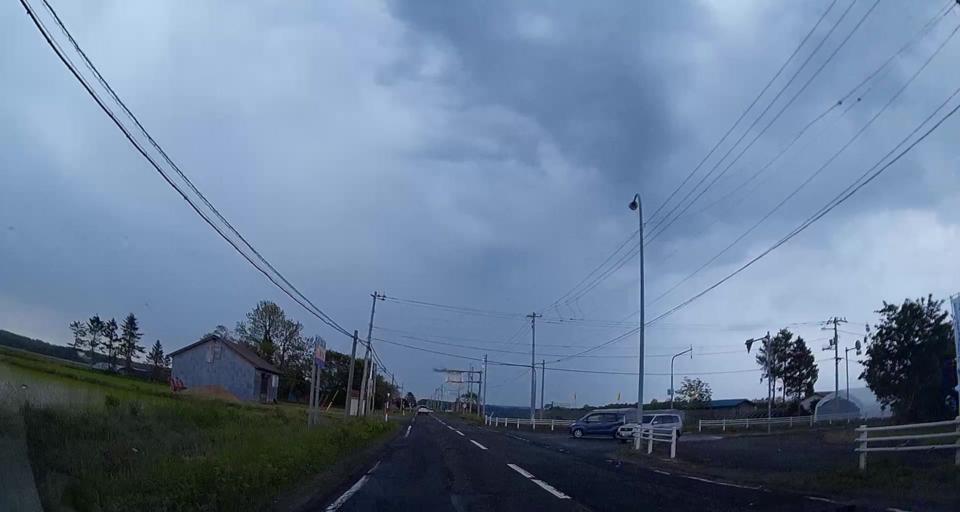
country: JP
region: Hokkaido
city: Chitose
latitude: 42.6976
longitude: 141.8476
